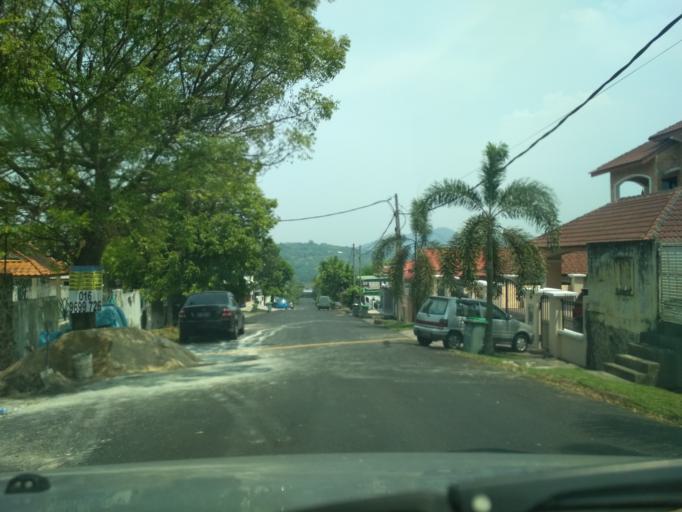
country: MY
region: Kedah
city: Kulim
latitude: 5.3558
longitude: 100.5275
